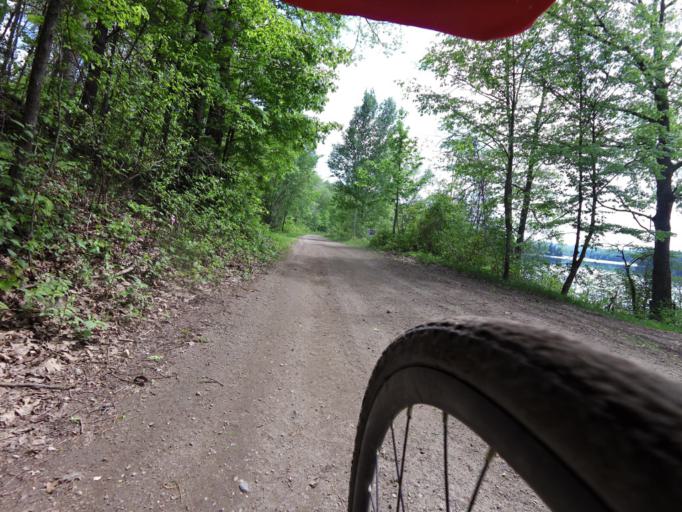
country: CA
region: Ontario
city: Renfrew
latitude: 45.1972
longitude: -76.6848
